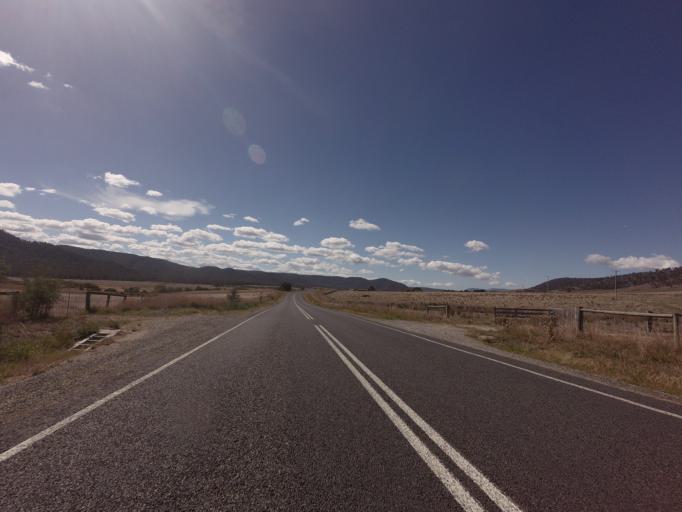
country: AU
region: Tasmania
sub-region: Break O'Day
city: St Helens
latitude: -41.7052
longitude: 147.8491
